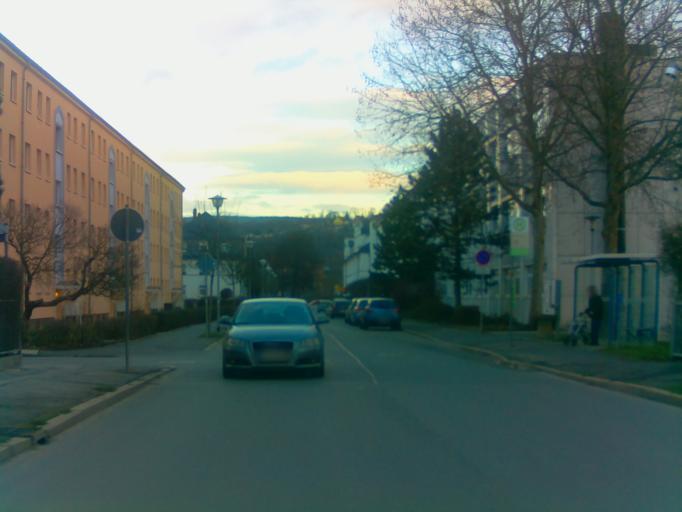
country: DE
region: Thuringia
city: Rudolstadt
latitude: 50.7146
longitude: 11.3460
